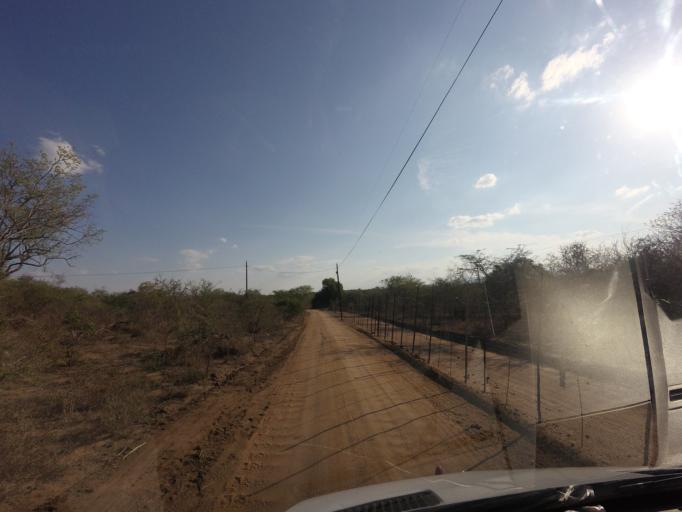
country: ZA
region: Limpopo
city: Thulamahashi
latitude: -24.5173
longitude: 31.1135
